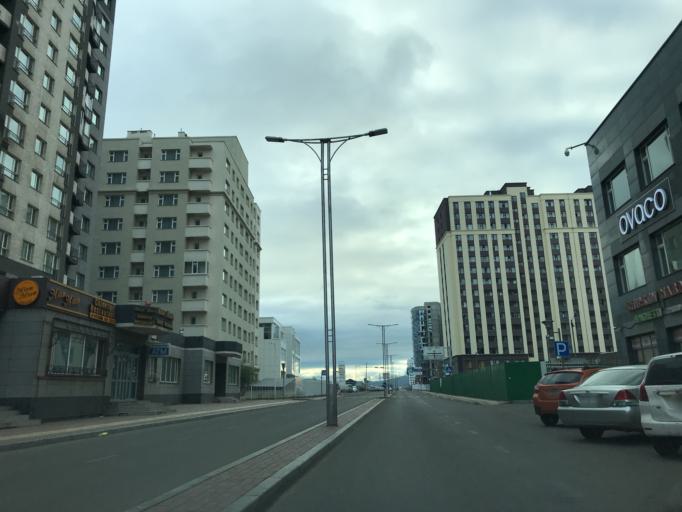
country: MN
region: Ulaanbaatar
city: Ulaanbaatar
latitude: 47.9048
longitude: 106.9408
